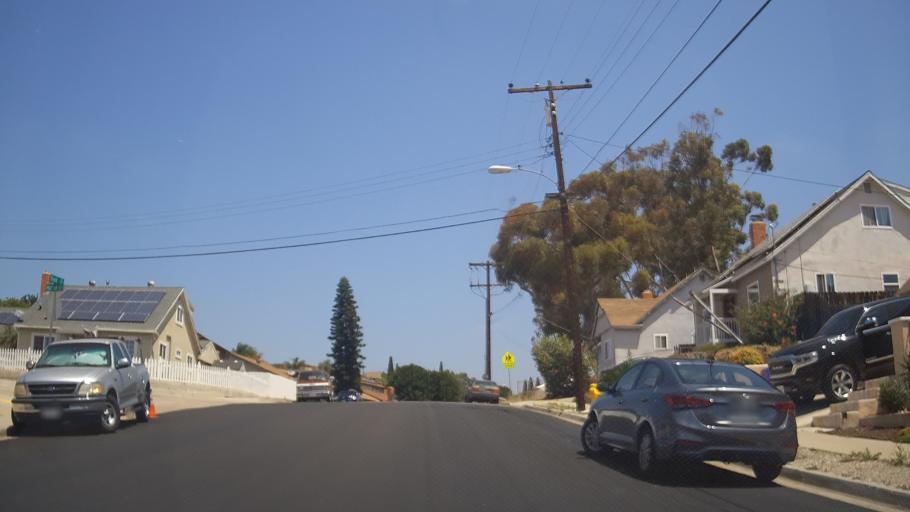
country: US
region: California
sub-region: San Diego County
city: Bonita
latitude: 32.6726
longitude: -117.0480
